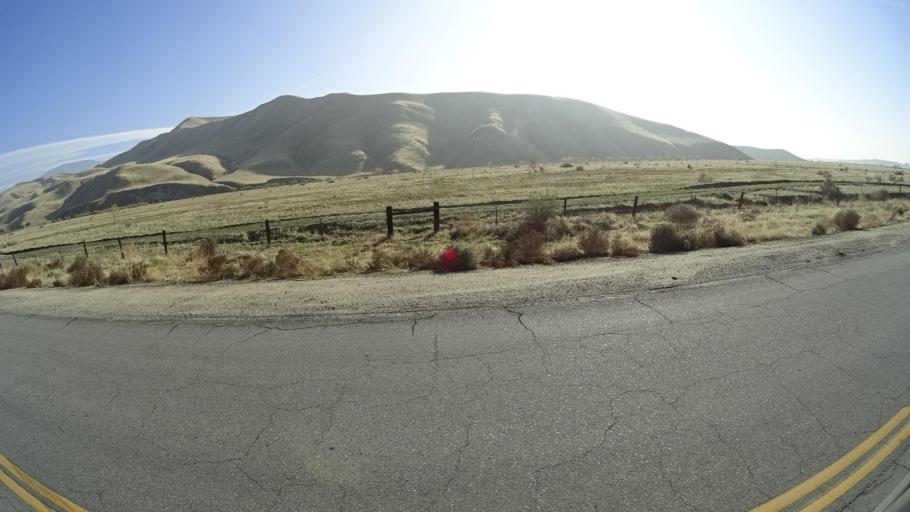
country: US
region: California
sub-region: Kern County
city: Arvin
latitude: 35.3264
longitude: -118.7400
